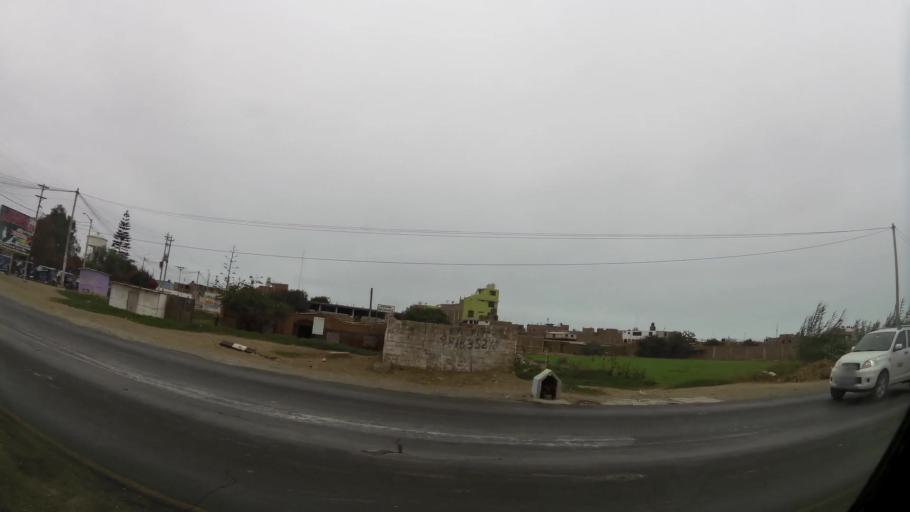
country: PE
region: La Libertad
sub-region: Provincia de Trujillo
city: Moche
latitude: -8.1675
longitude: -79.0067
